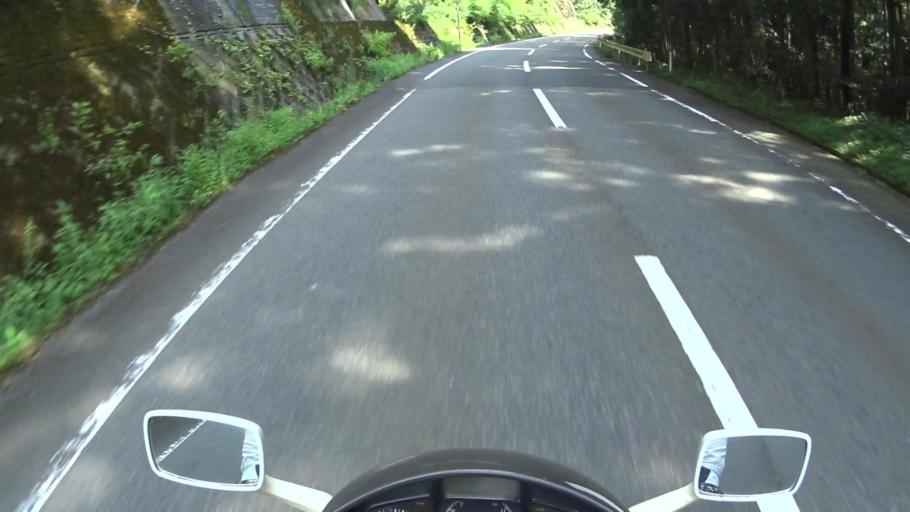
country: JP
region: Fukui
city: Obama
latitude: 35.2727
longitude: 135.5924
